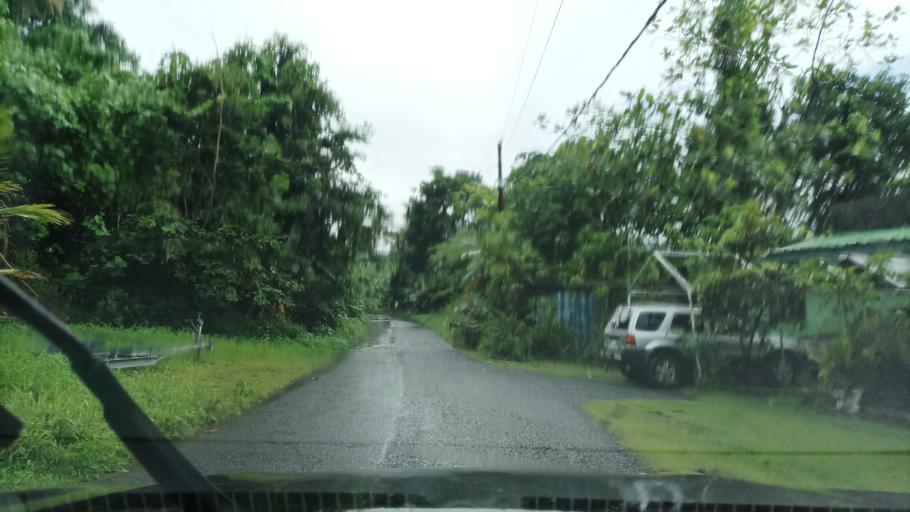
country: FM
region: Pohnpei
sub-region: Kolonia Municipality
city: Kolonia
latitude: 6.9560
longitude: 158.2268
